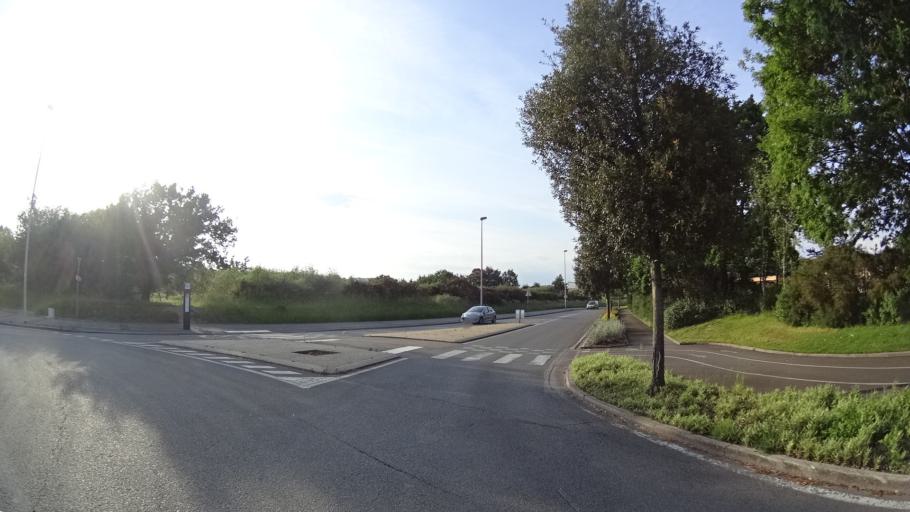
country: FR
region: Brittany
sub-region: Departement du Morbihan
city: Vannes
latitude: 47.6496
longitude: -2.7441
